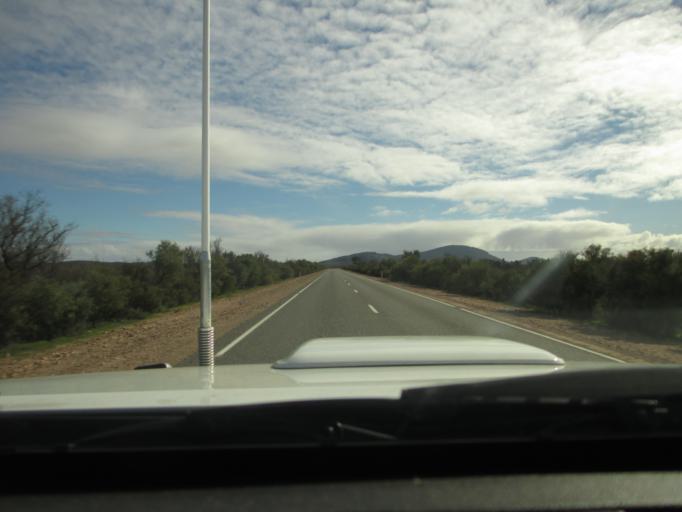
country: AU
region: South Australia
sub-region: Flinders Ranges
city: Quorn
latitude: -31.8353
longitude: 138.3878
